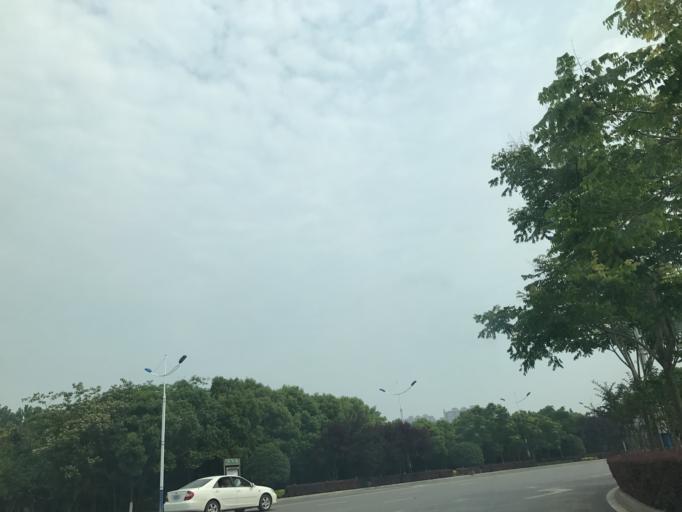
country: CN
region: Hubei
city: Houkou
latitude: 30.6391
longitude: 113.1336
